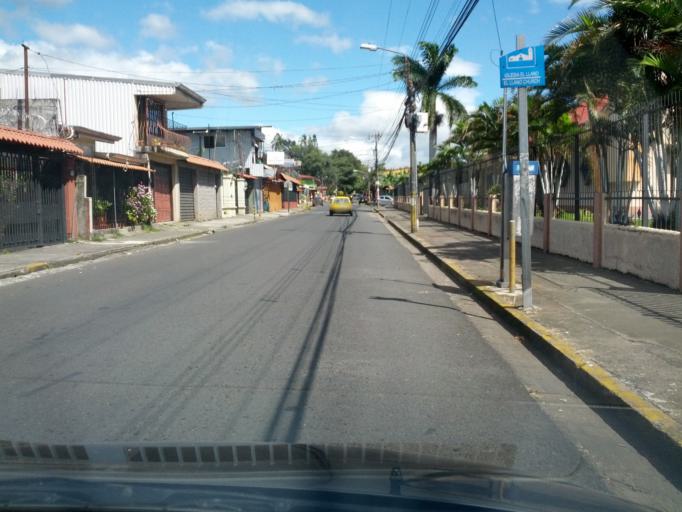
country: CR
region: Alajuela
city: Alajuela
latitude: 10.0205
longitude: -84.2073
